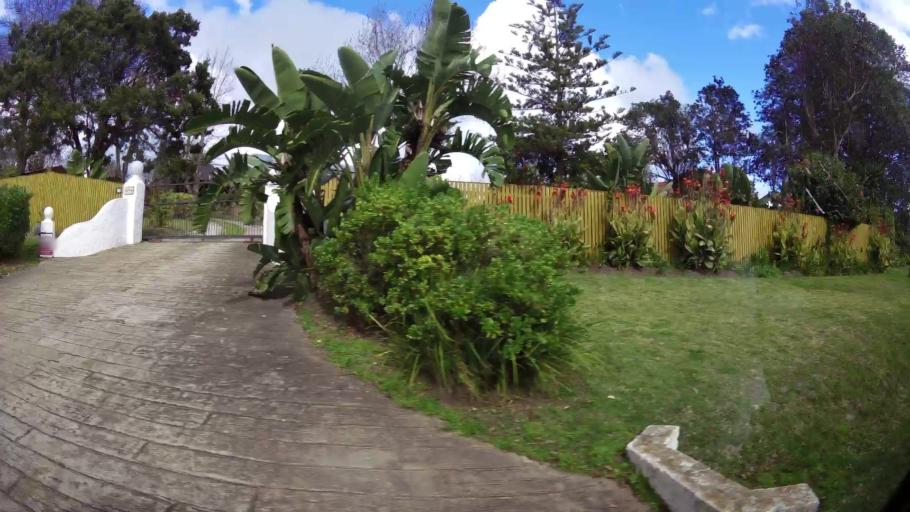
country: ZA
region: Western Cape
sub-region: Eden District Municipality
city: Knysna
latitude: -34.0613
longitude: 23.0809
